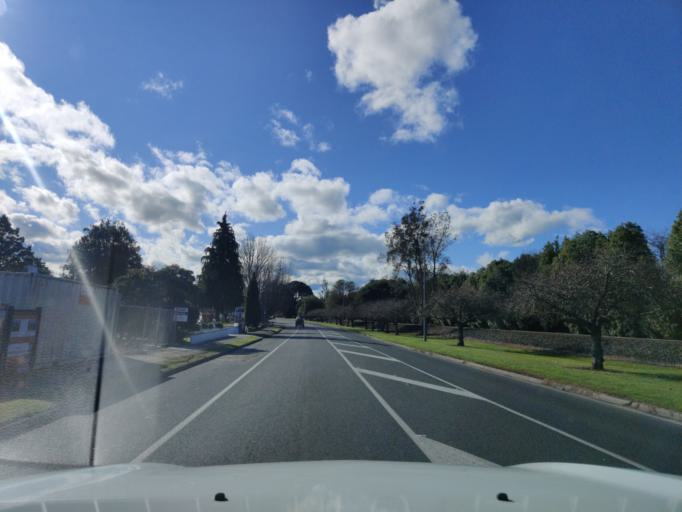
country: NZ
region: Waikato
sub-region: Matamata-Piako District
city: Matamata
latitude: -37.8229
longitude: 175.7708
